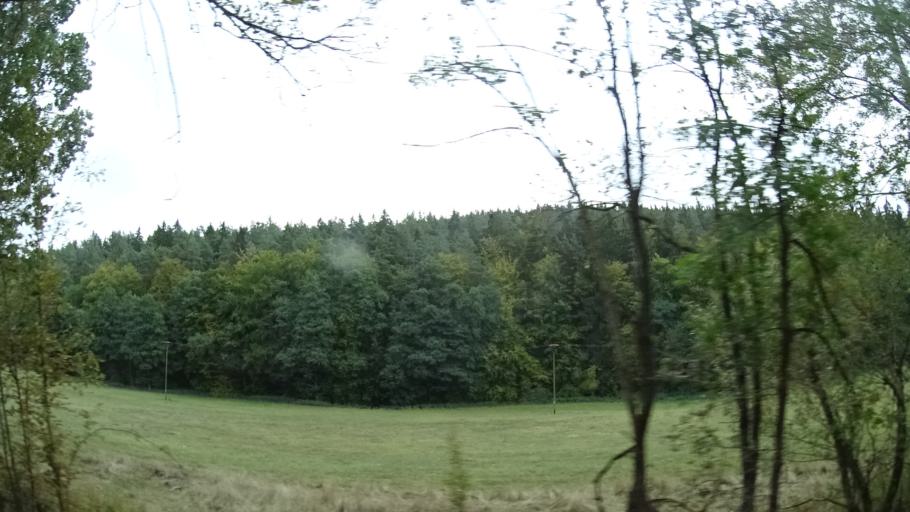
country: DE
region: Thuringia
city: Wahns
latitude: 50.6305
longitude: 10.2768
